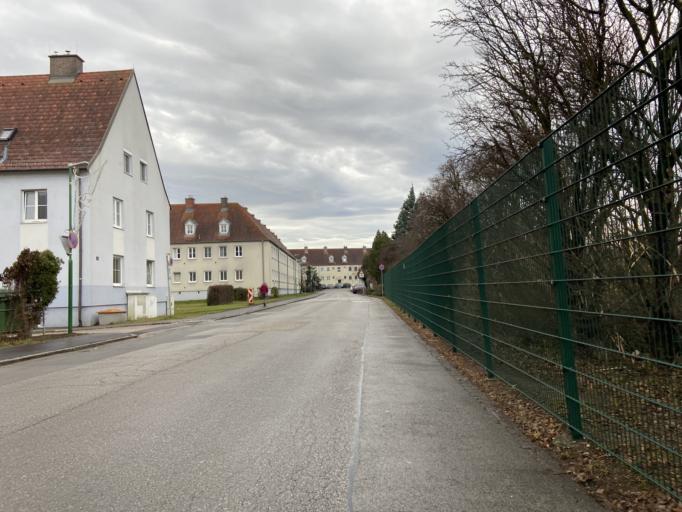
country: AT
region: Lower Austria
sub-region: Politischer Bezirk Modling
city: Neu-Guntramsdorf
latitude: 48.0655
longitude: 16.3157
